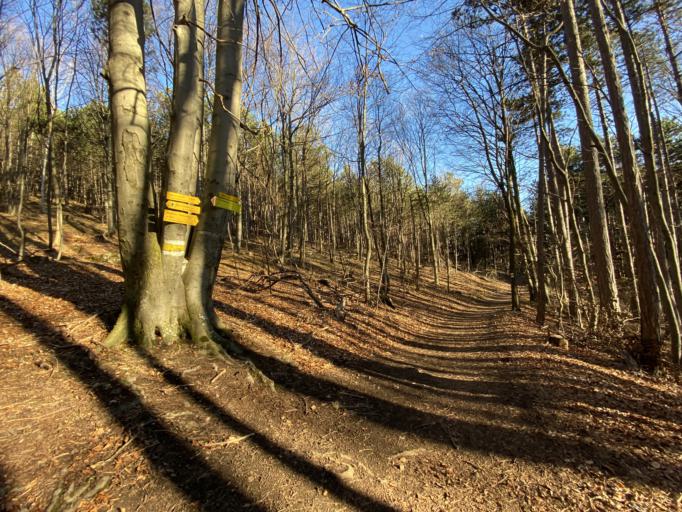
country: AT
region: Lower Austria
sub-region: Politischer Bezirk Baden
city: Bad Voslau
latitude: 47.9886
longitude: 16.1630
